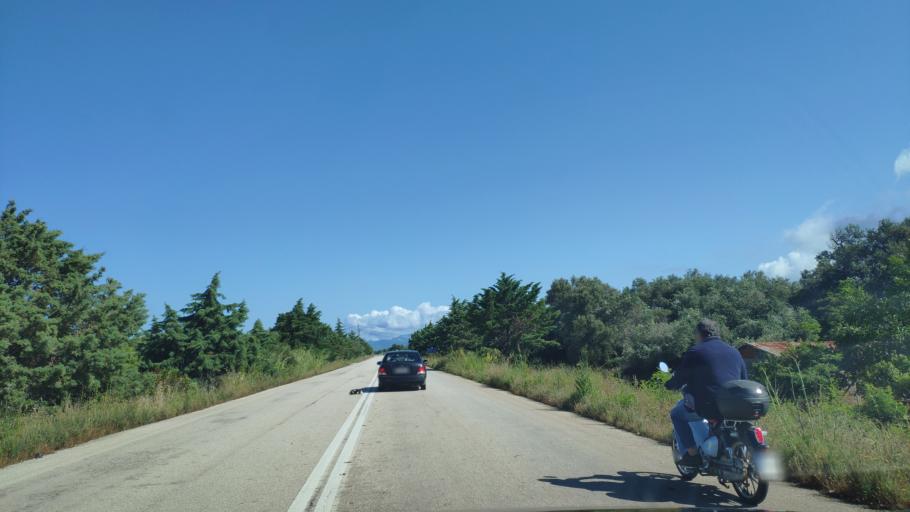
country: GR
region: Epirus
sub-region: Nomos Prevezis
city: Preveza
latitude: 38.9669
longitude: 20.7247
